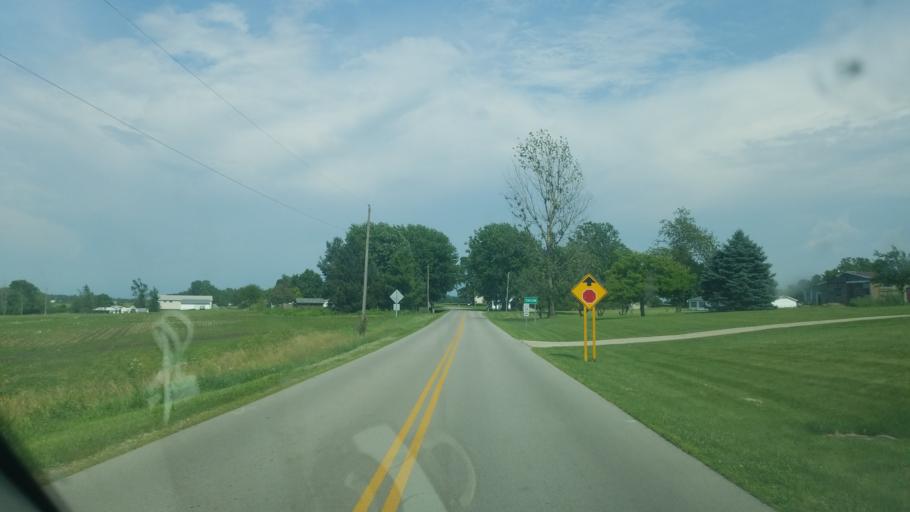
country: US
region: Ohio
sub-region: Logan County
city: West Liberty
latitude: 40.3000
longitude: -83.6641
